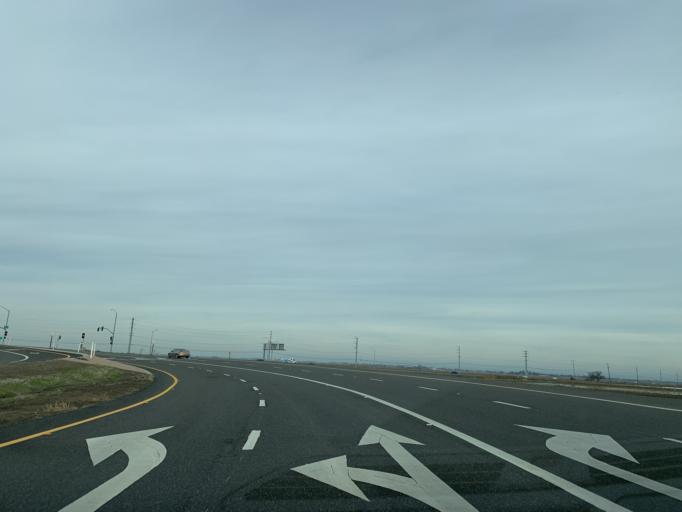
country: US
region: California
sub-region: Sacramento County
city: Elverta
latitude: 38.7128
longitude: -121.5386
